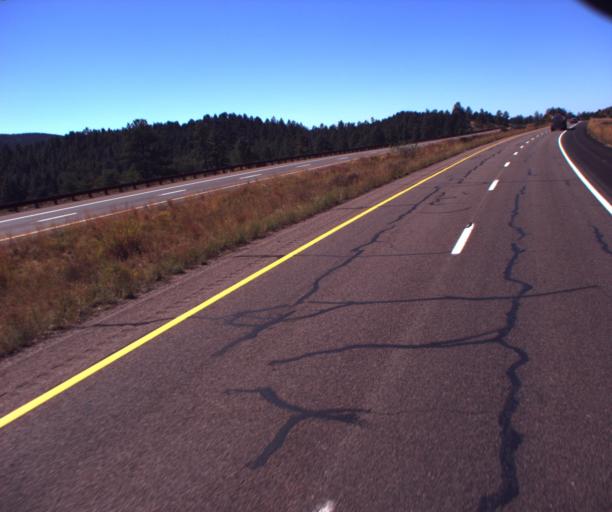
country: US
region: Arizona
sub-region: Gila County
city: Star Valley
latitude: 34.2803
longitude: -111.1512
